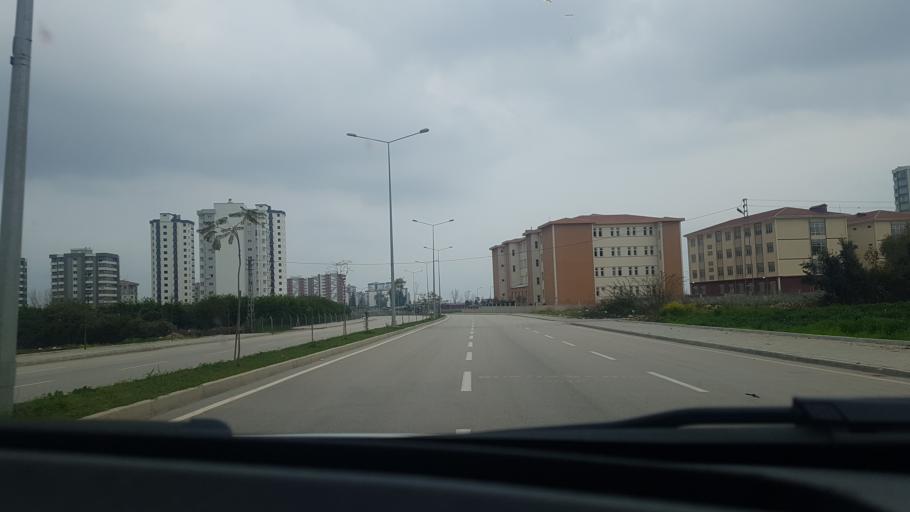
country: TR
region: Adana
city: Seyhan
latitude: 37.0128
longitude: 35.2569
